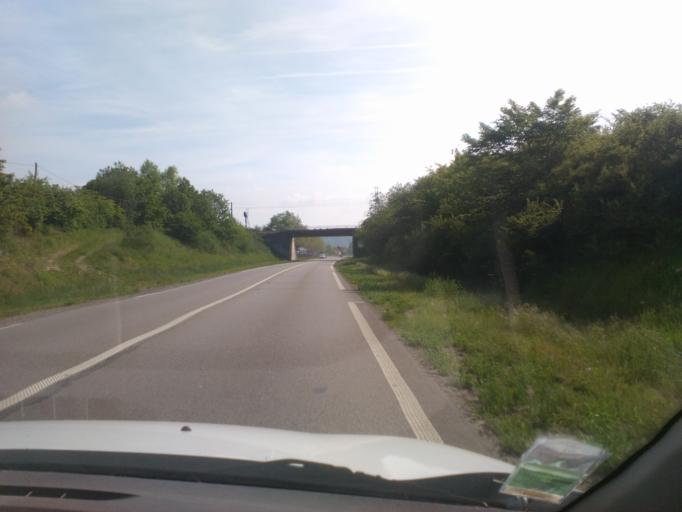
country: FR
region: Lorraine
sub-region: Departement des Vosges
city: Chavelot
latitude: 48.2182
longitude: 6.4263
